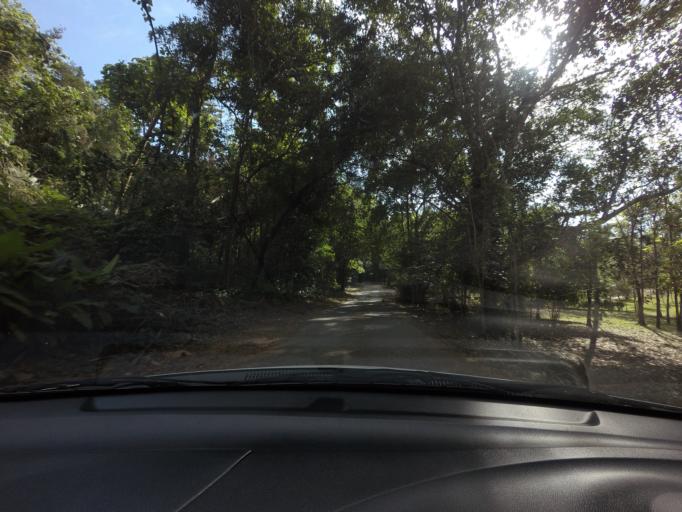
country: TH
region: Nakhon Nayok
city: Nakhon Nayok
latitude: 14.3304
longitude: 101.3068
